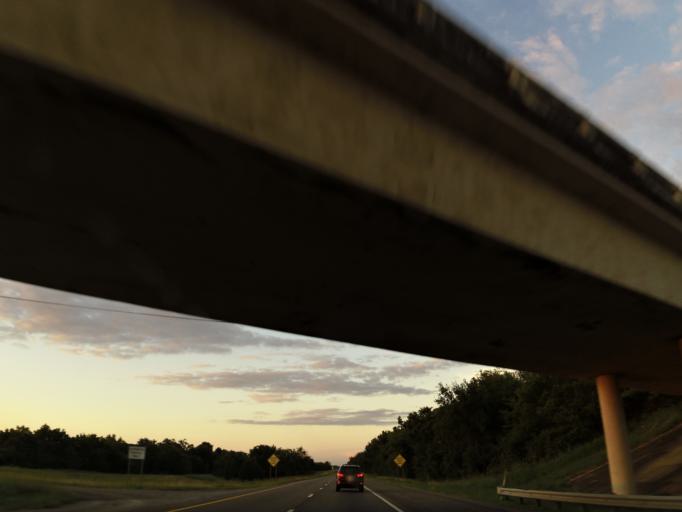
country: US
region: Tennessee
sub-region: Monroe County
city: Sweetwater
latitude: 35.6656
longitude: -84.4525
